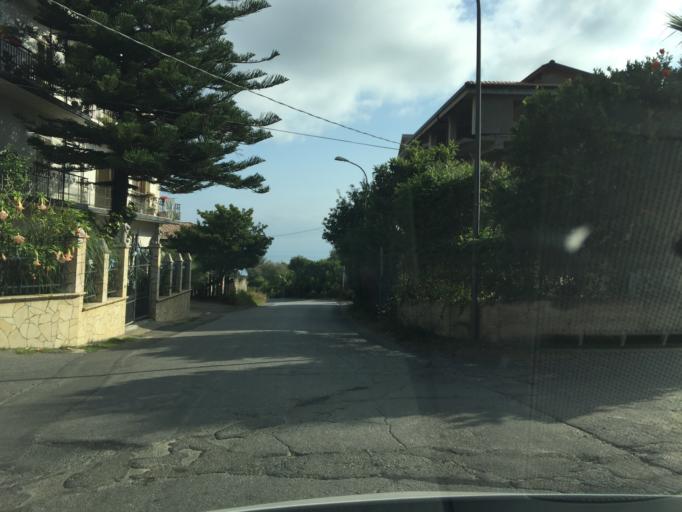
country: IT
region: Calabria
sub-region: Provincia di Vibo-Valentia
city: Pannaconi
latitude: 38.6930
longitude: 16.0446
